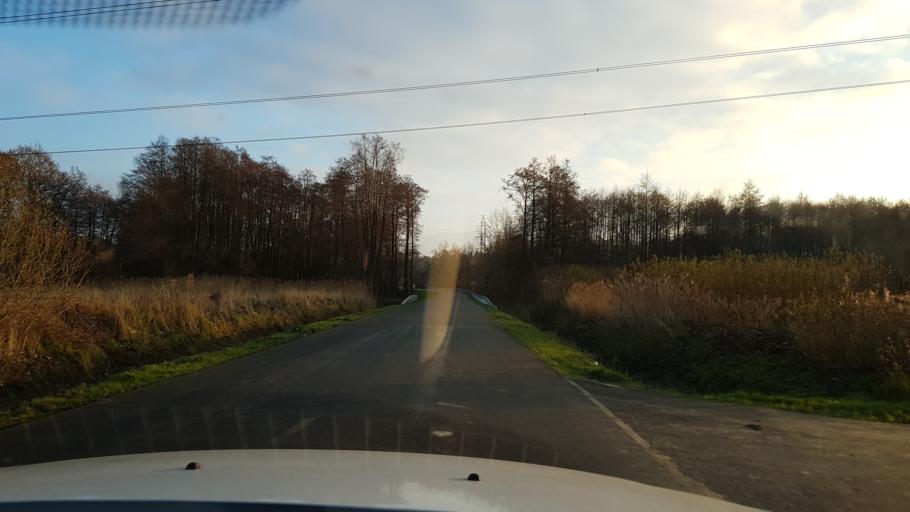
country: PL
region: West Pomeranian Voivodeship
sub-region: Koszalin
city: Koszalin
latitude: 54.1252
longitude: 16.0906
